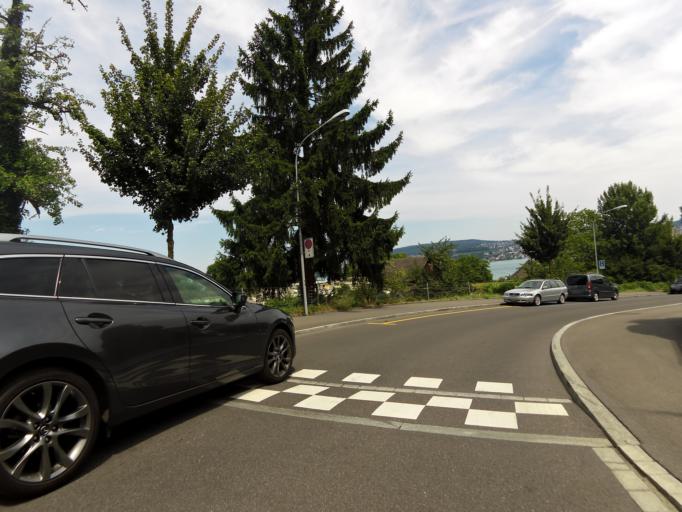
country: CH
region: Zurich
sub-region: Bezirk Zuerich
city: Zuerich (Kreis 2) / Wollishofen
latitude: 47.3377
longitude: 8.5346
